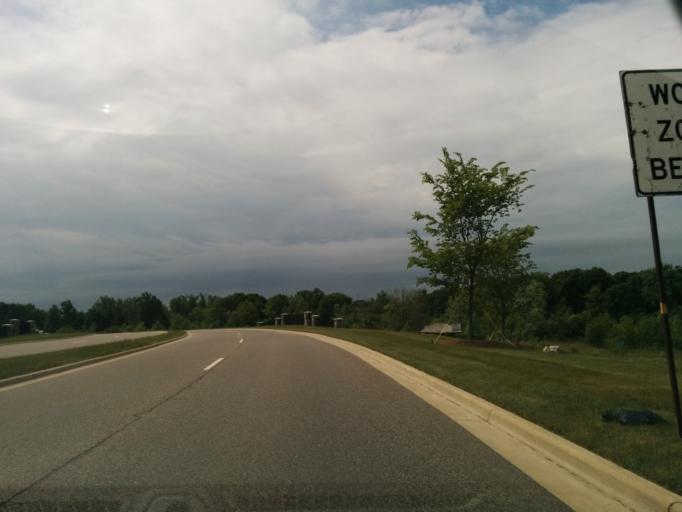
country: US
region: Michigan
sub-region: Oakland County
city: Wolverine Lake
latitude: 42.5635
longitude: -83.4513
